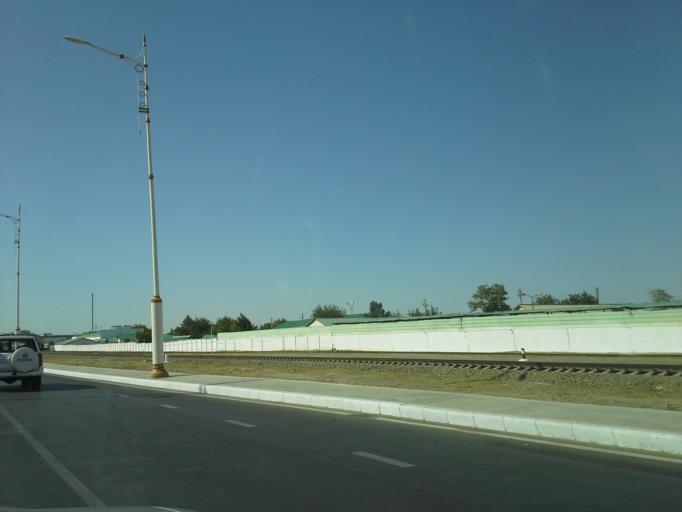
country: TM
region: Ahal
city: Ashgabat
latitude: 37.9315
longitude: 58.4178
